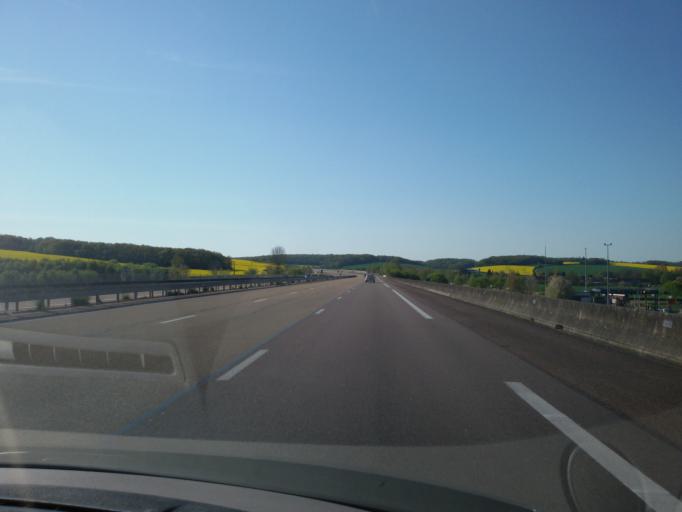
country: FR
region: Bourgogne
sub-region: Departement de l'Yonne
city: Saint-Julien-du-Sault
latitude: 47.9411
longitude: 3.2422
